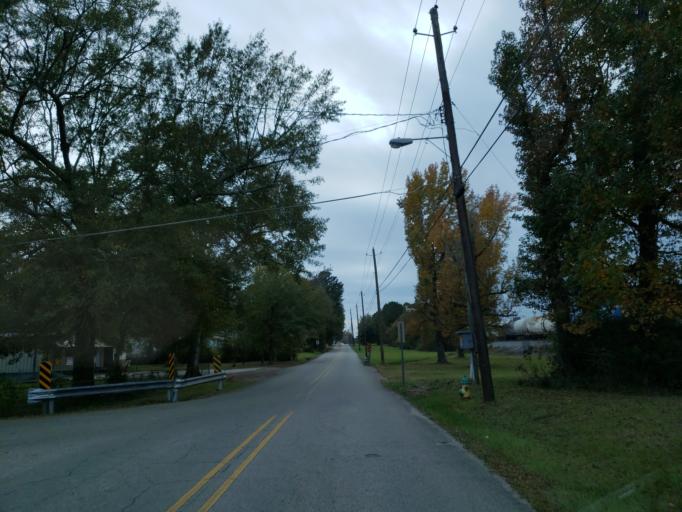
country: US
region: Mississippi
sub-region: Forrest County
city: Hattiesburg
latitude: 31.3163
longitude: -89.2993
